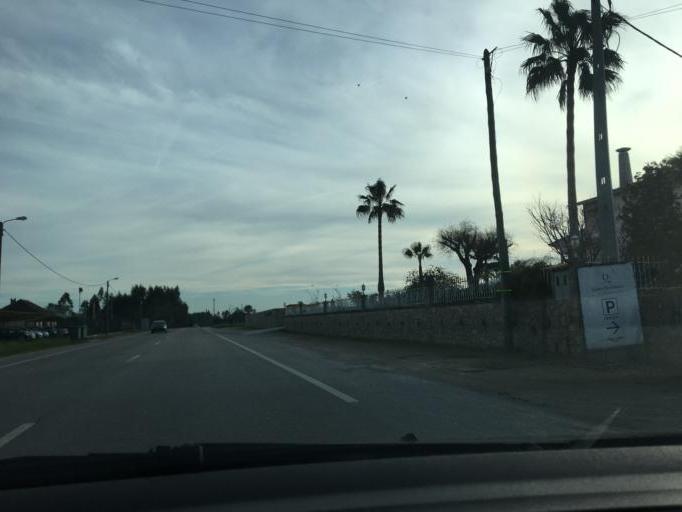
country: PT
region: Coimbra
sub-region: Soure
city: Alfarelos
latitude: 40.2158
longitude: -8.6038
